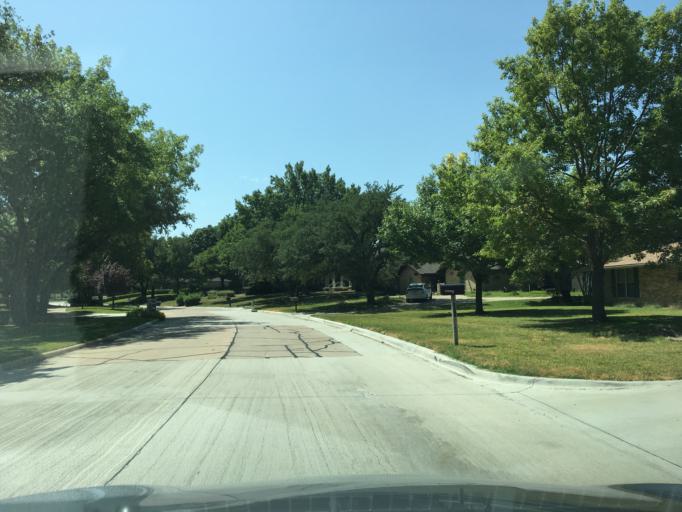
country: US
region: Texas
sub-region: Dallas County
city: Garland
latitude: 32.8755
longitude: -96.6058
